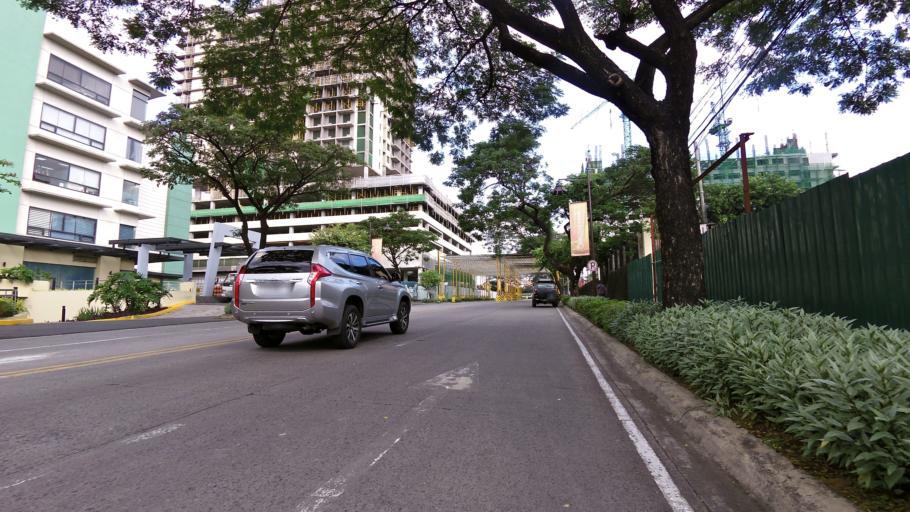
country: PH
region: Metro Manila
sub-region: Pasig
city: Pasig City
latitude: 14.5873
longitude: 121.0776
